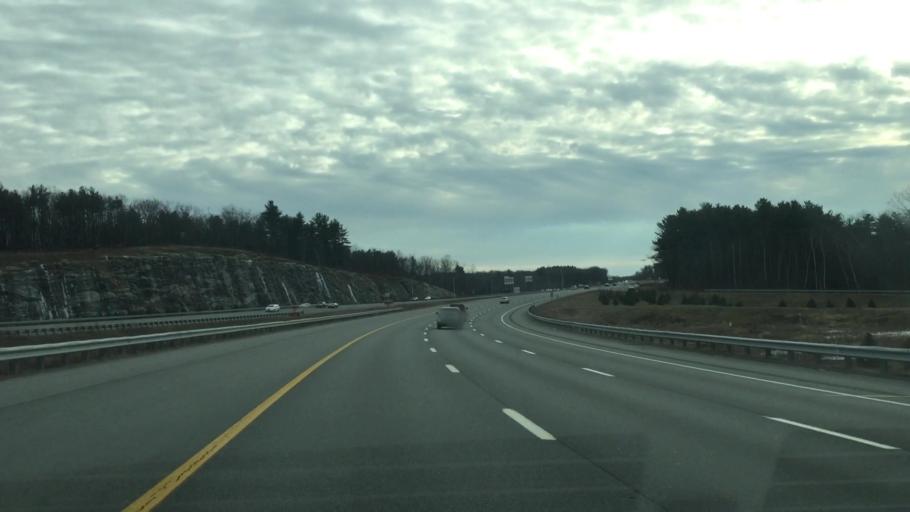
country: US
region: New Hampshire
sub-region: Rockingham County
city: Windham
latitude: 42.8074
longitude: -71.2715
